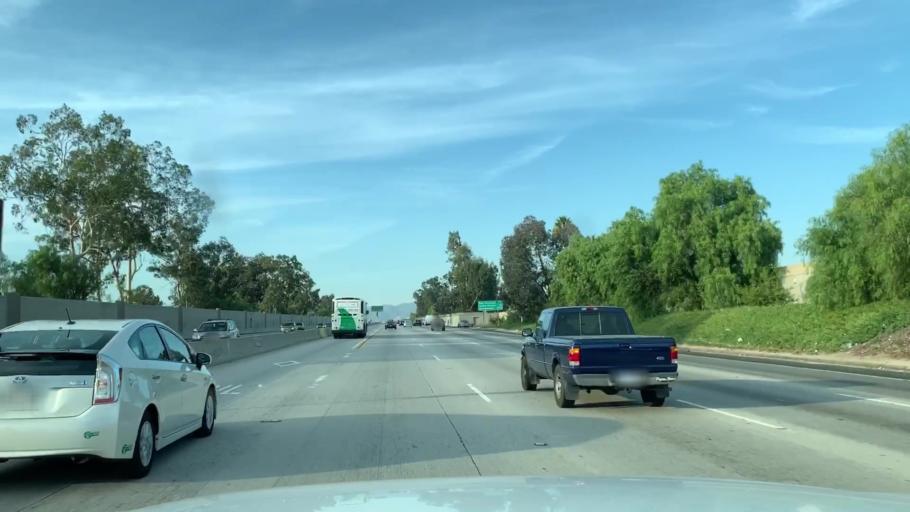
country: US
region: California
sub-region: Los Angeles County
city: North Hollywood
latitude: 34.2109
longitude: -118.4072
